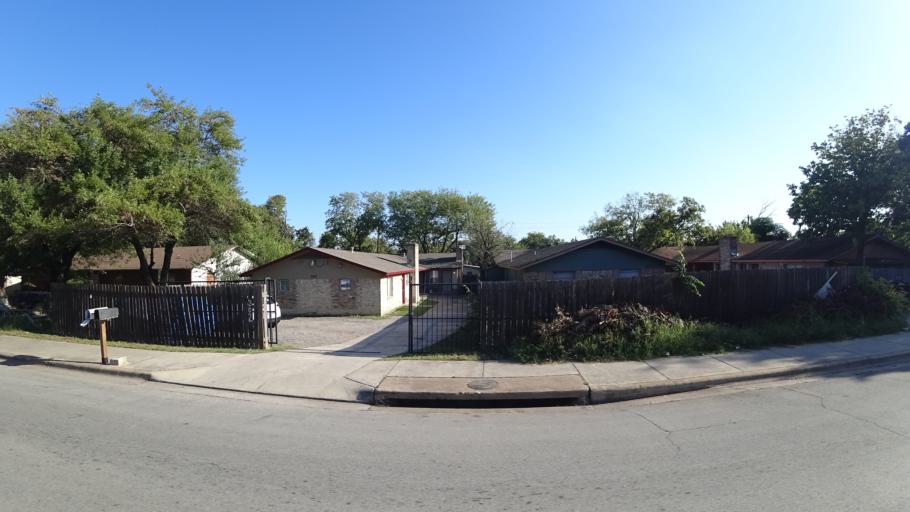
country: US
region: Texas
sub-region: Travis County
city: Austin
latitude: 30.3465
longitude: -97.7010
